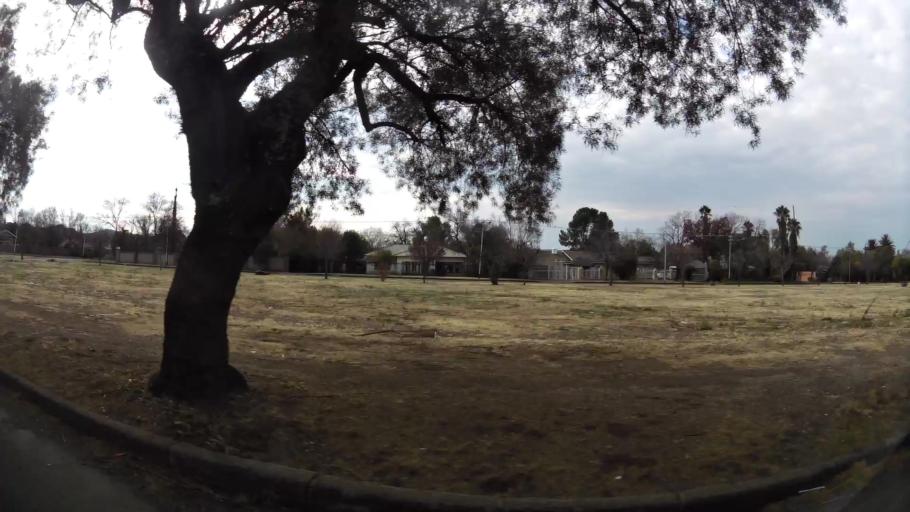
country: ZA
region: Orange Free State
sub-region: Mangaung Metropolitan Municipality
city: Bloemfontein
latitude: -29.0900
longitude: 26.2409
